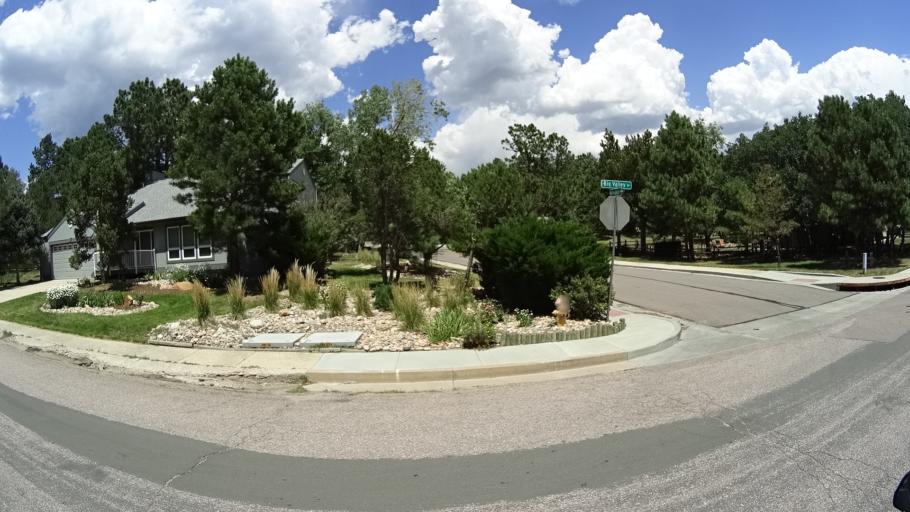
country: US
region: Colorado
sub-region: El Paso County
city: Air Force Academy
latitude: 38.9371
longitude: -104.8470
